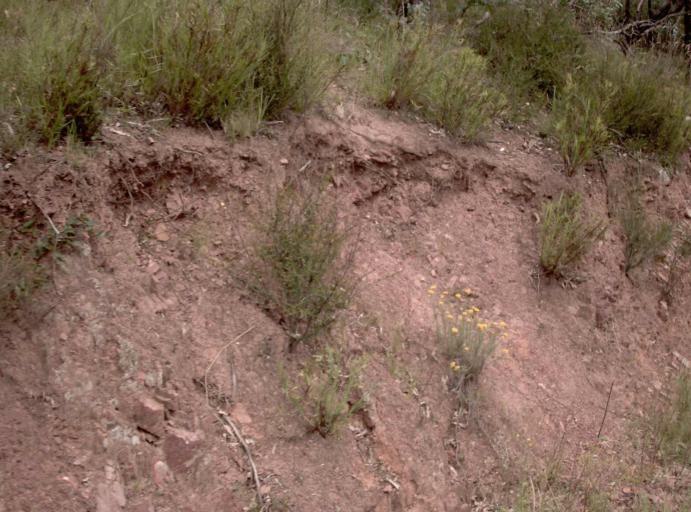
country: AU
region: Victoria
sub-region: Wellington
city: Heyfield
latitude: -37.7148
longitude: 146.6689
